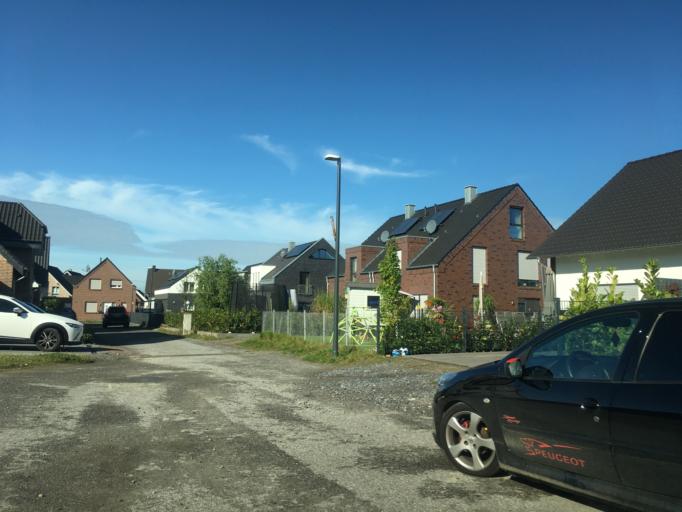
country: DE
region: North Rhine-Westphalia
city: Ludinghausen
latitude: 51.7800
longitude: 7.4647
